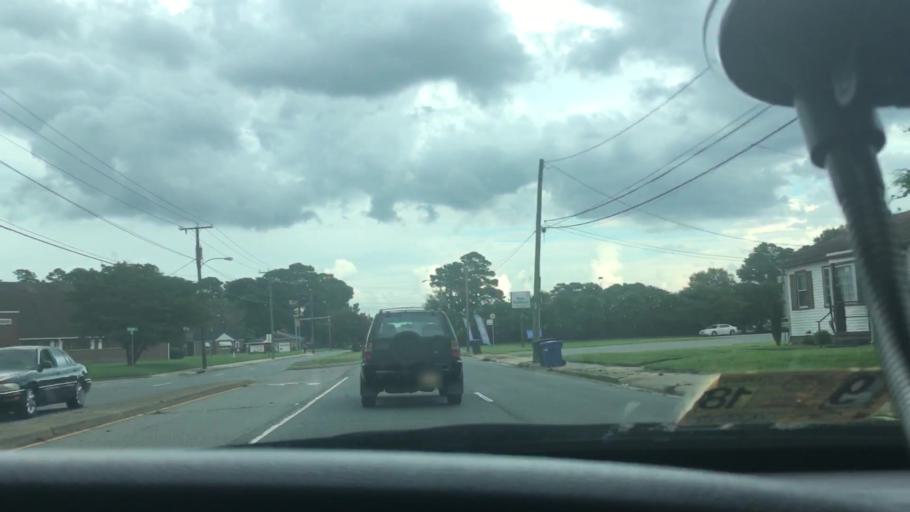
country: US
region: Virginia
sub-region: City of Portsmouth
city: Portsmouth Heights
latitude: 36.8209
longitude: -76.3877
